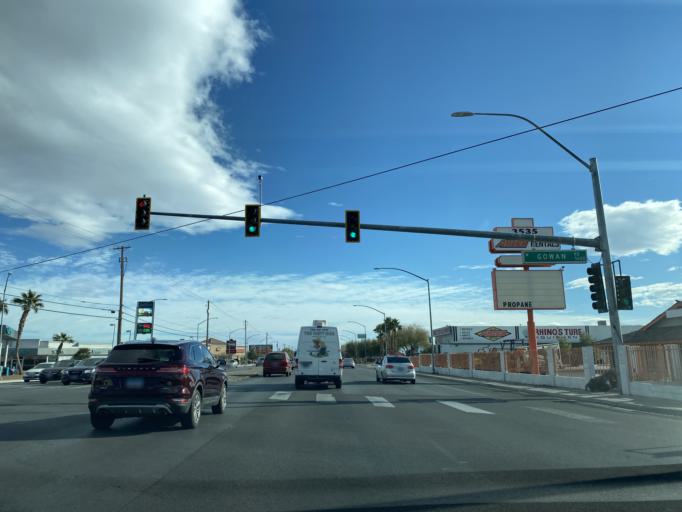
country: US
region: Nevada
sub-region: Clark County
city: Las Vegas
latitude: 36.2244
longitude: -115.2189
